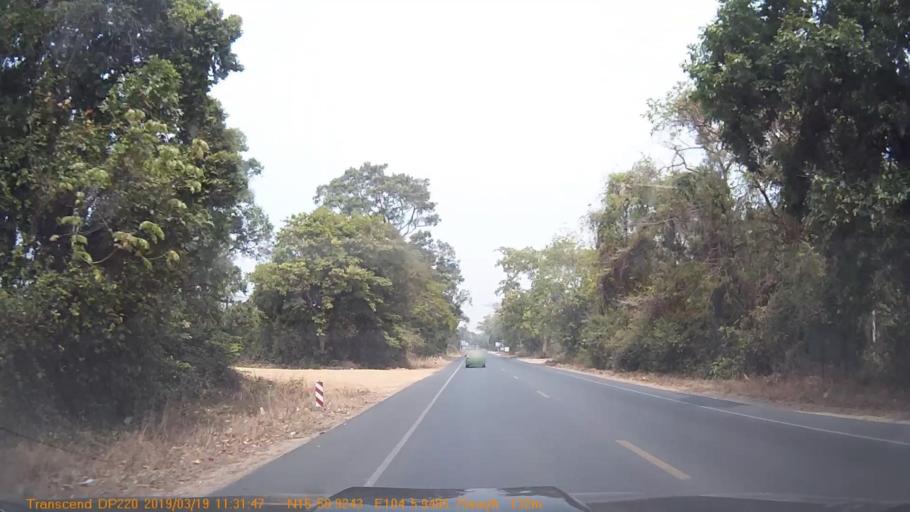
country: TH
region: Yasothon
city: Yasothon
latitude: 15.8491
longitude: 104.0989
